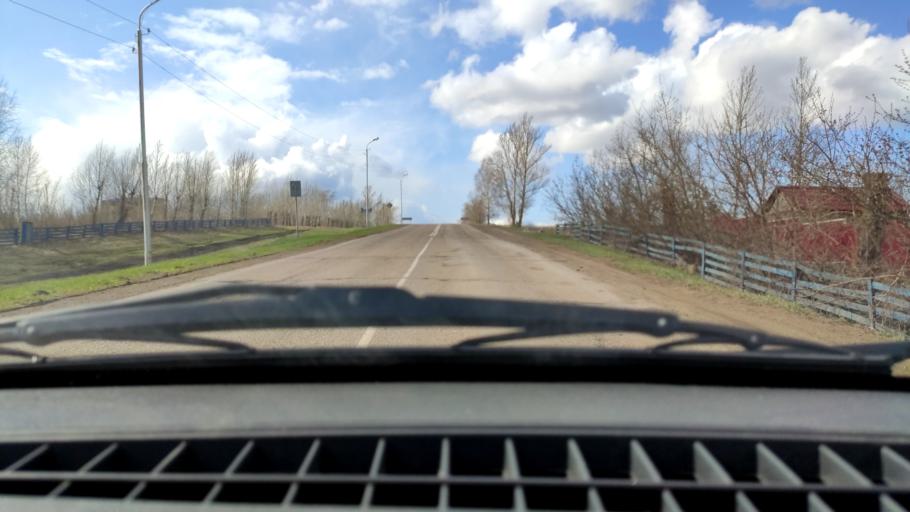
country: RU
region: Bashkortostan
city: Kushnarenkovo
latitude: 55.0936
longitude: 55.0554
